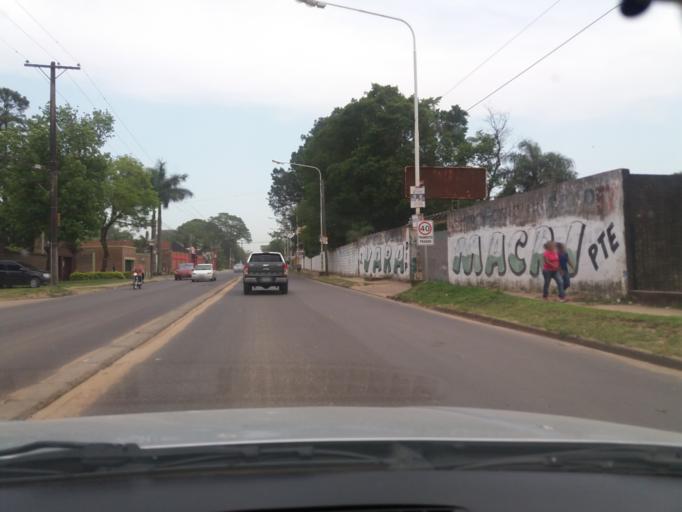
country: AR
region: Corrientes
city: Corrientes
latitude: -27.5043
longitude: -58.8118
